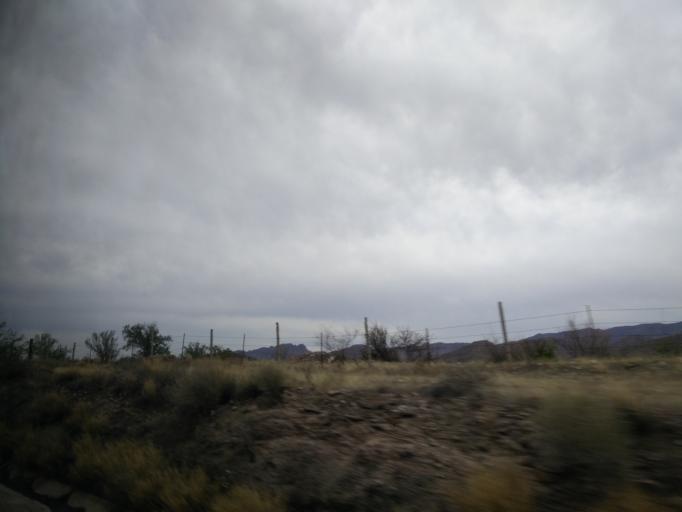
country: MX
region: Sonora
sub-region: Hermosillo
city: Miguel Aleman (La Doce)
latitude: 28.5190
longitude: -111.0461
